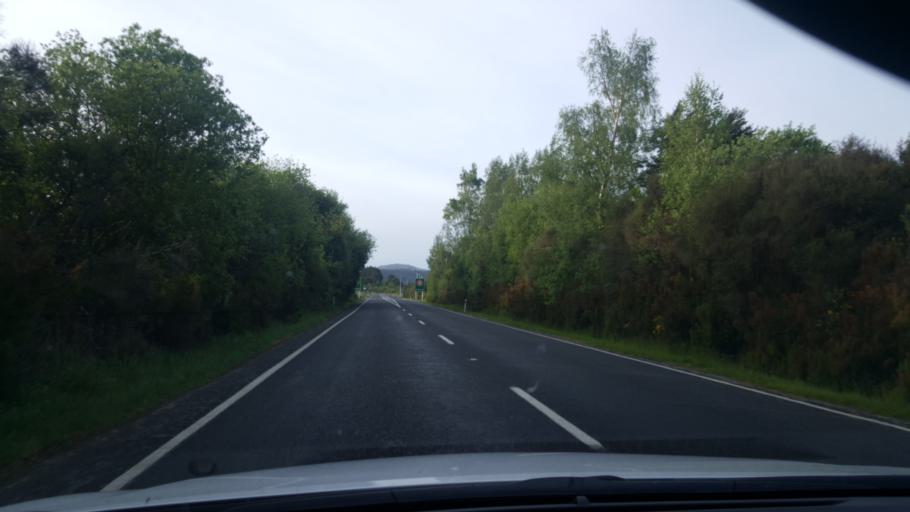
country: NZ
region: Waikato
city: Turangi
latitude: -38.9669
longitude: 175.7676
